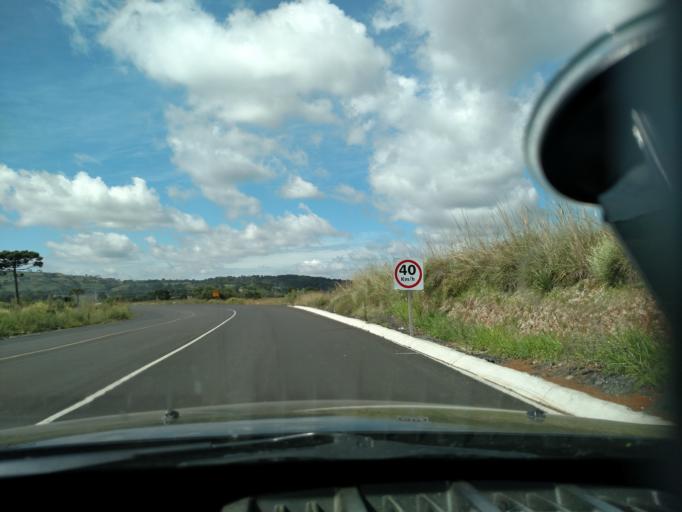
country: BR
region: Santa Catarina
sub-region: Sao Joaquim
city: Sao Joaquim
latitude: -28.1093
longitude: -50.0513
